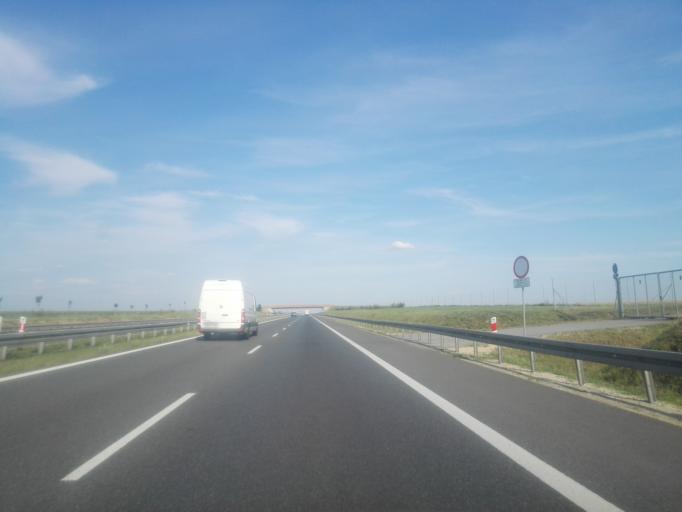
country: PL
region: Lower Silesian Voivodeship
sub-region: Powiat olesnicki
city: Dobroszyce
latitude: 51.2276
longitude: 17.2645
